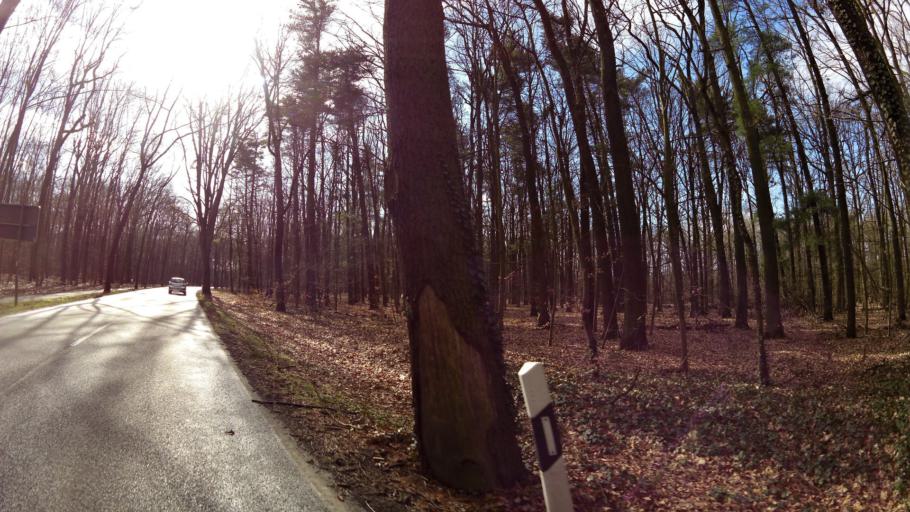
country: DE
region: Brandenburg
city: Konigs Wusterhausen
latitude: 52.2901
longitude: 13.6492
